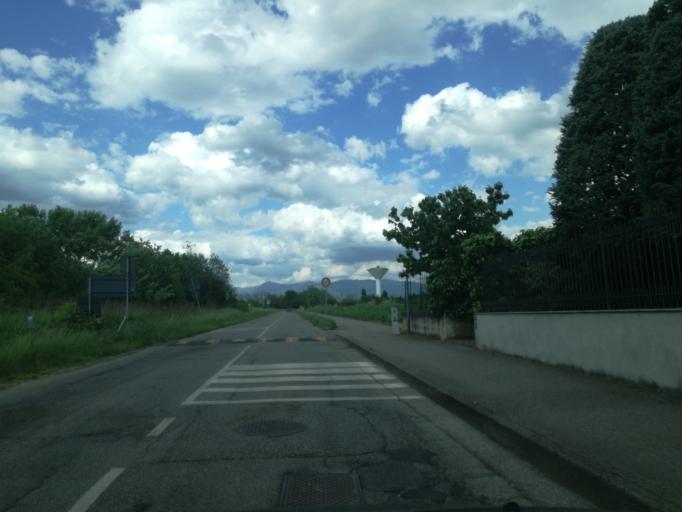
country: IT
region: Lombardy
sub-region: Provincia di Monza e Brianza
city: Carnate
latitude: 45.6540
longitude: 9.3834
